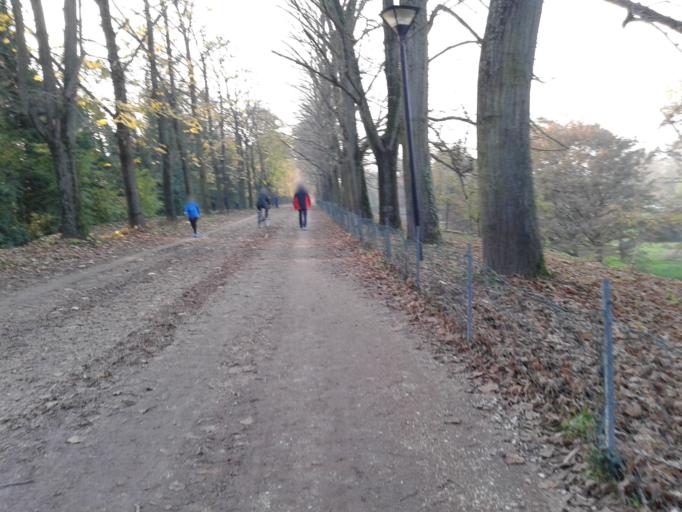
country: IT
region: Emilia-Romagna
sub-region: Provincia di Ferrara
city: Ferrara
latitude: 44.8489
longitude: 11.6285
